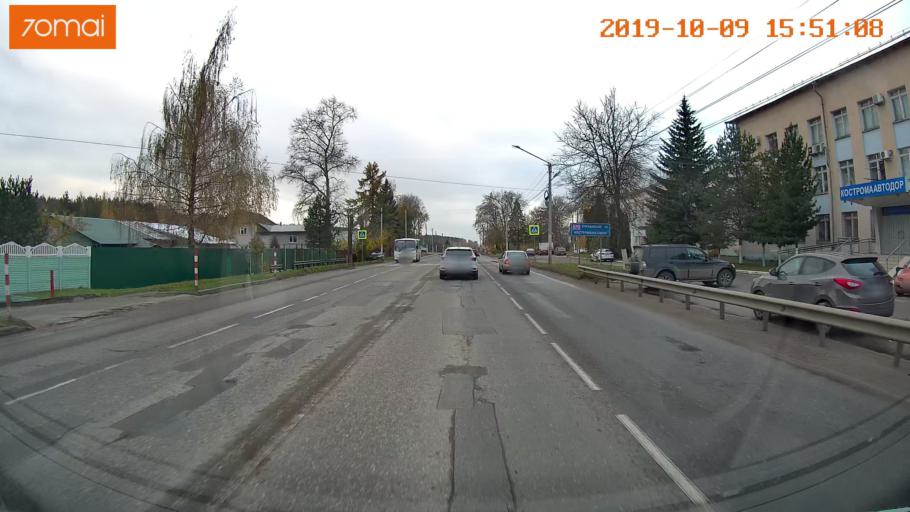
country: RU
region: Kostroma
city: Oktyabr'skiy
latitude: 57.7993
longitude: 40.9818
